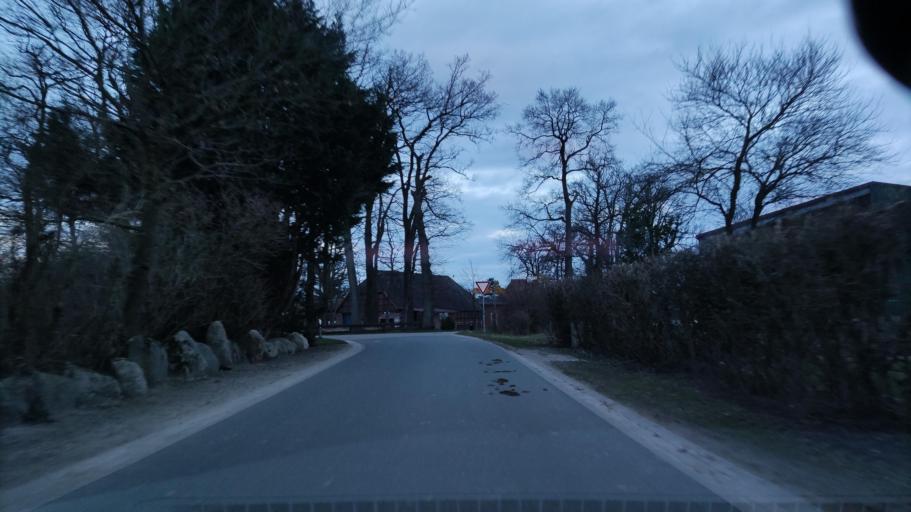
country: DE
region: Lower Saxony
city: Natendorf
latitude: 53.0581
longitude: 10.4509
